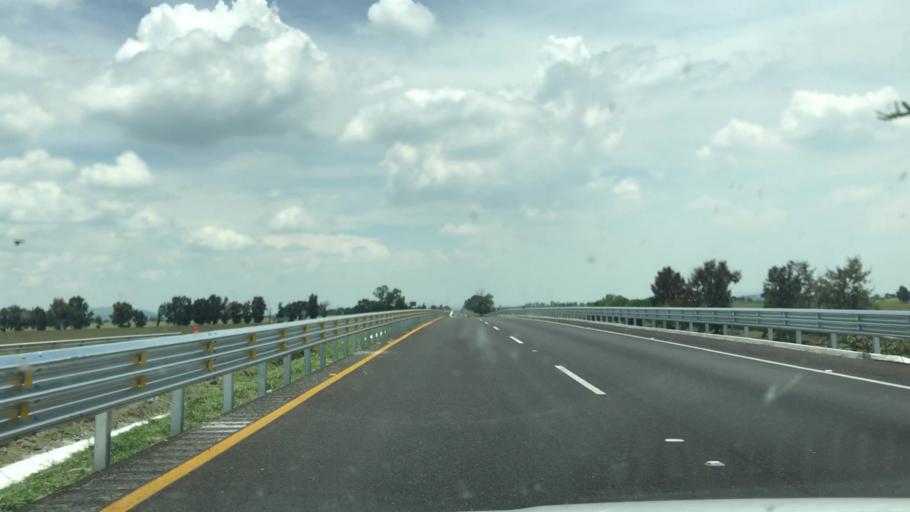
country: MX
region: Guanajuato
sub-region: Salamanca
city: San Vicente de Flores
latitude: 20.6364
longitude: -101.2591
